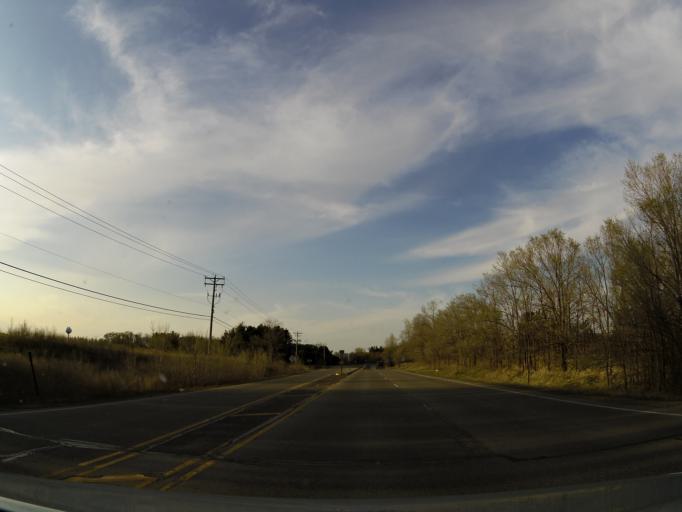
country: US
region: Minnesota
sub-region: Washington County
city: Lakeland
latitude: 44.9441
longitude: -92.7314
